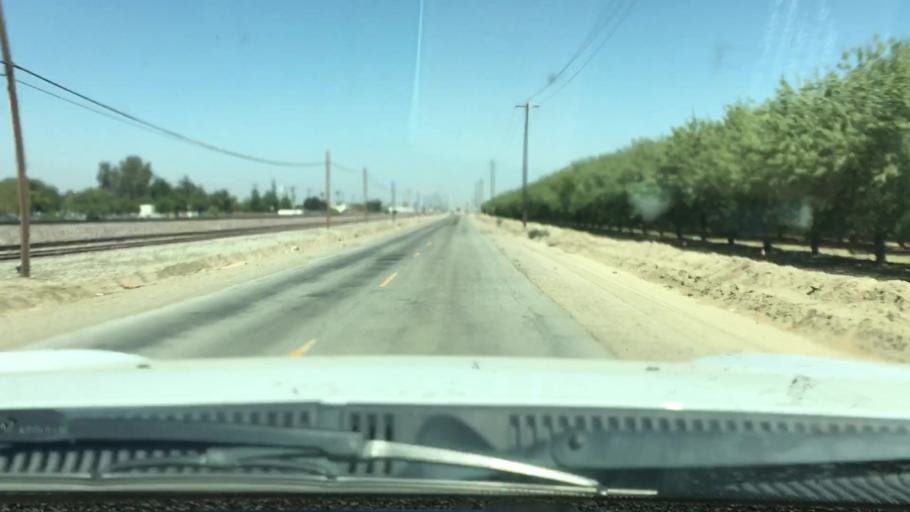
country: US
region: California
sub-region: Kern County
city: Wasco
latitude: 35.5724
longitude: -119.3318
